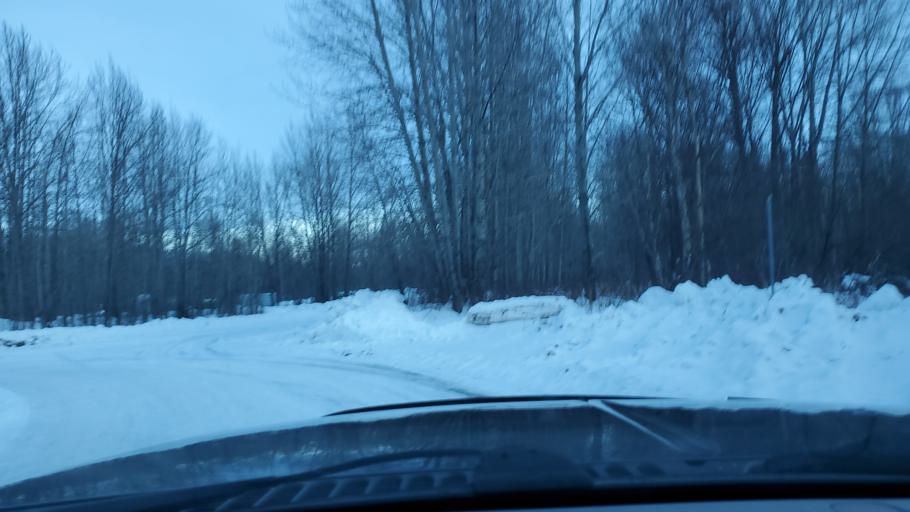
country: US
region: Alaska
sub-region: Matanuska-Susitna Borough
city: Lazy Mountain
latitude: 61.7078
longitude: -148.8962
